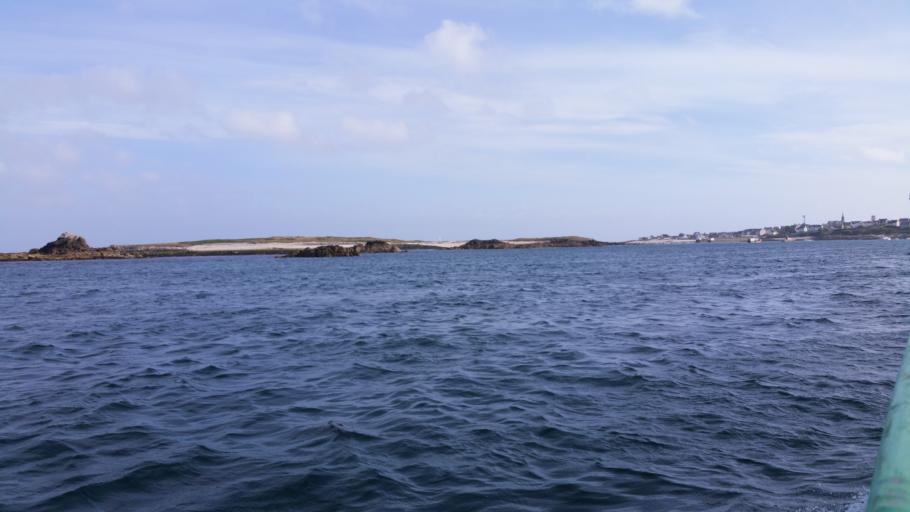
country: FR
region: Brittany
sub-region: Departement du Finistere
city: Le Conquet
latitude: 48.4078
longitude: -4.9522
